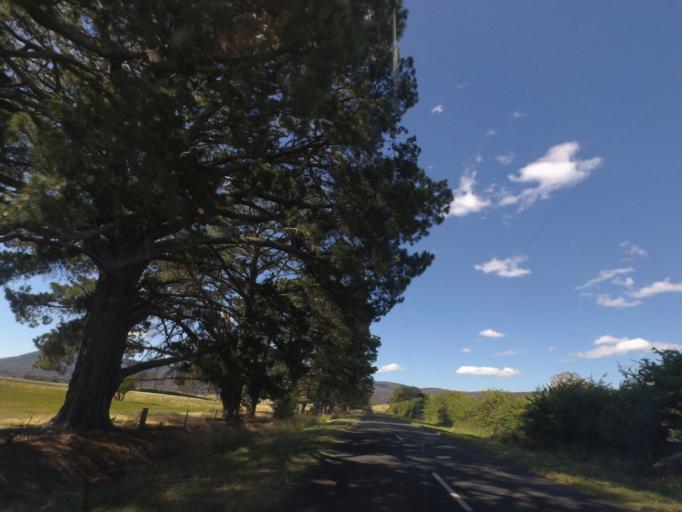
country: AU
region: Victoria
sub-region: Hume
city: Sunbury
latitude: -37.4424
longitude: 144.6050
